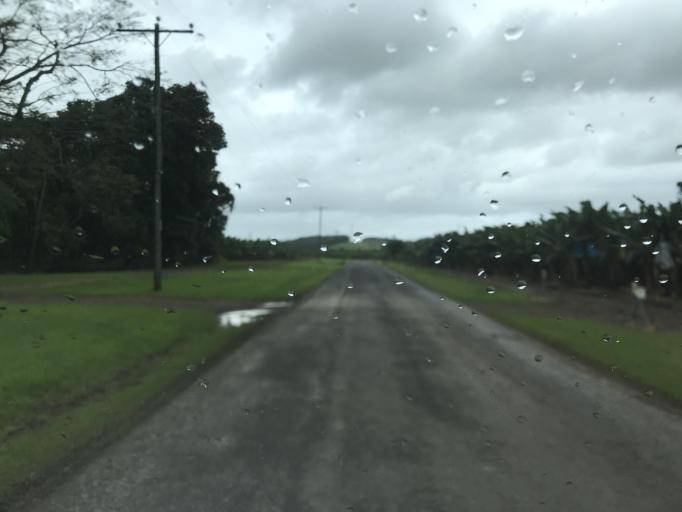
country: AU
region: Queensland
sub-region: Cassowary Coast
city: Innisfail
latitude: -17.5032
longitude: 145.9810
